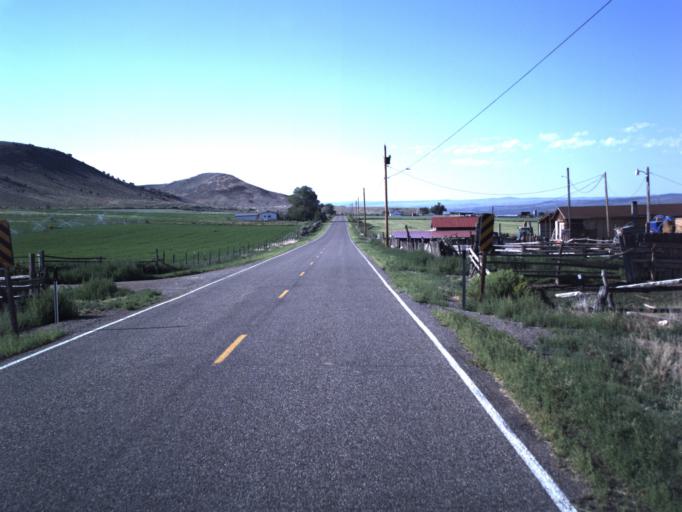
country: US
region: Utah
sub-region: Wayne County
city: Loa
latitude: 38.4474
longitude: -111.6158
